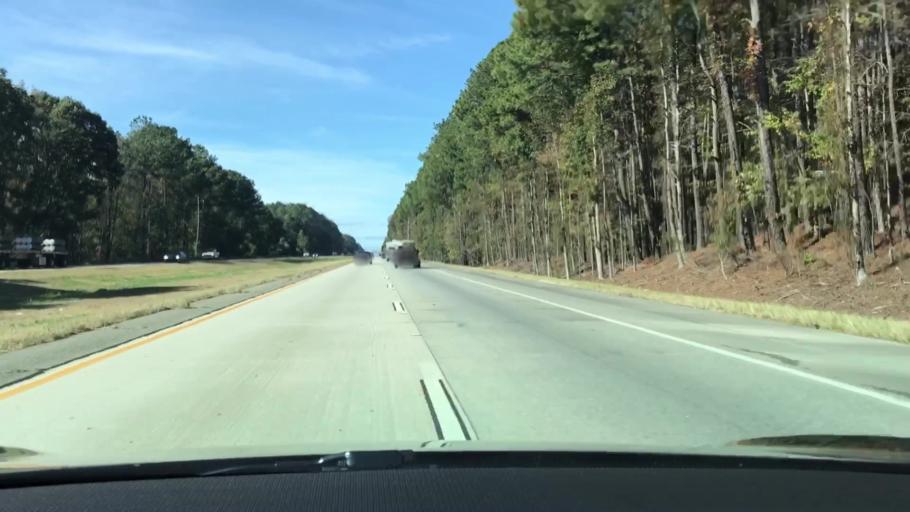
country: US
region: Georgia
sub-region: Greene County
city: Greensboro
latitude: 33.5488
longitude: -83.1508
